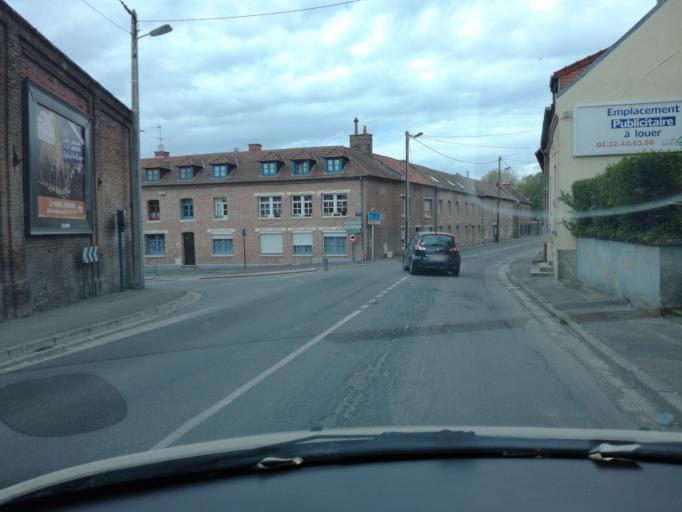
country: FR
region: Picardie
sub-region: Departement de la Somme
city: Saleux
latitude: 49.8555
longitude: 2.2393
